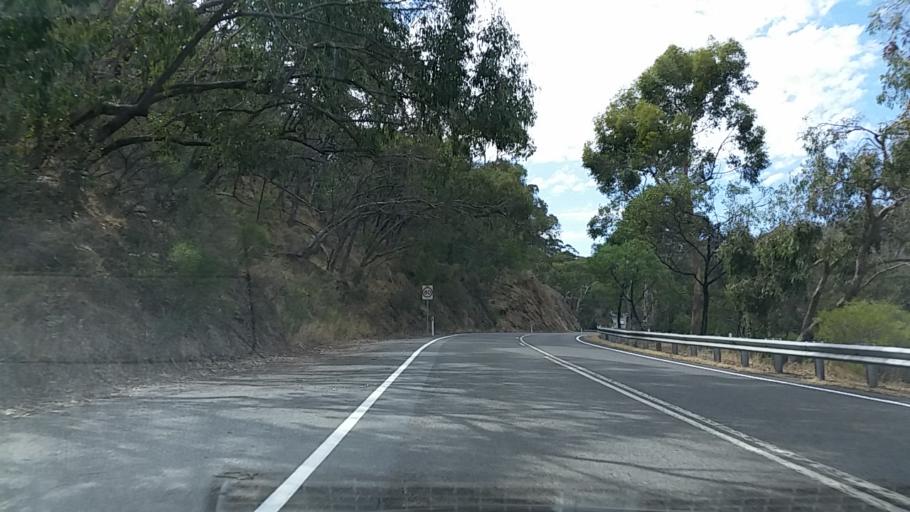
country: AU
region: South Australia
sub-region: Campbelltown
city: Athelstone
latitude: -34.8642
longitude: 138.7793
